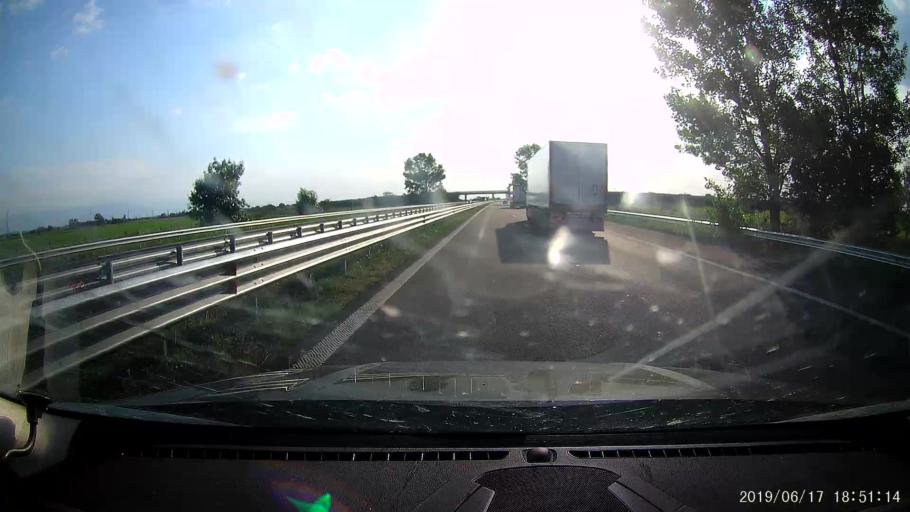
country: BG
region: Plovdiv
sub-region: Obshtina Rakovski
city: Rakovski
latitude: 42.2136
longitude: 24.9778
